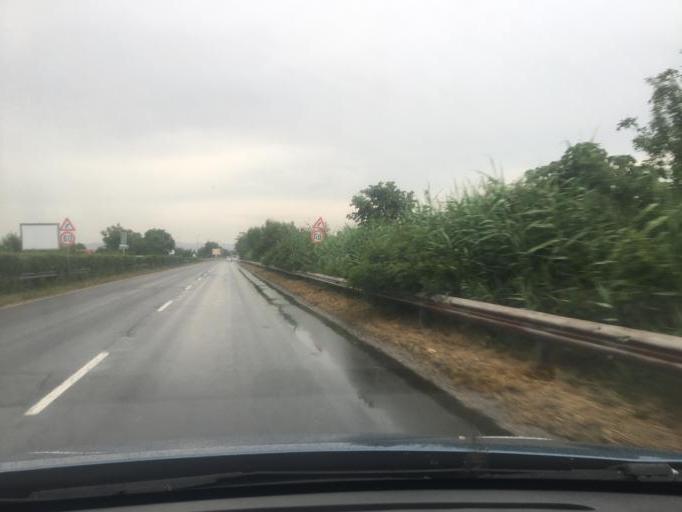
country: BG
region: Burgas
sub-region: Obshtina Burgas
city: Burgas
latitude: 42.5470
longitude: 27.4745
